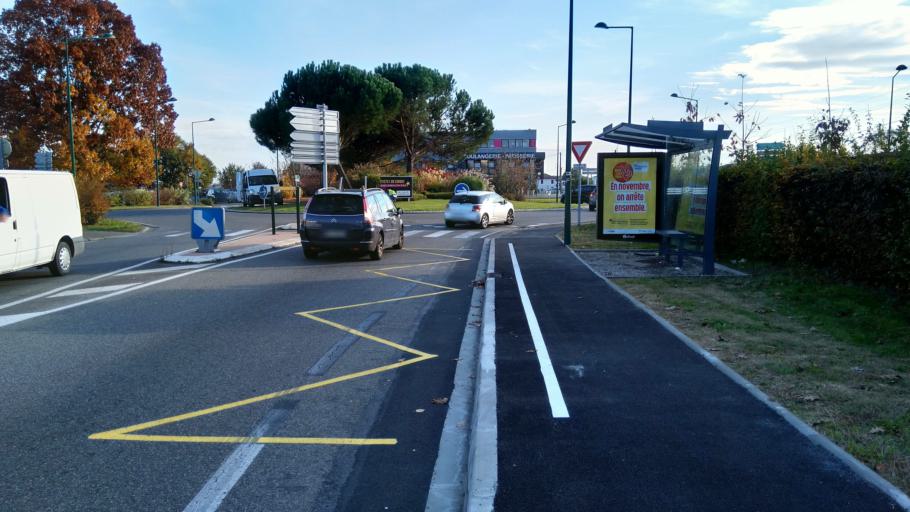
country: FR
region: Aquitaine
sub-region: Departement des Landes
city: Saint-Paul-les-Dax
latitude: 43.7369
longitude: -1.0513
